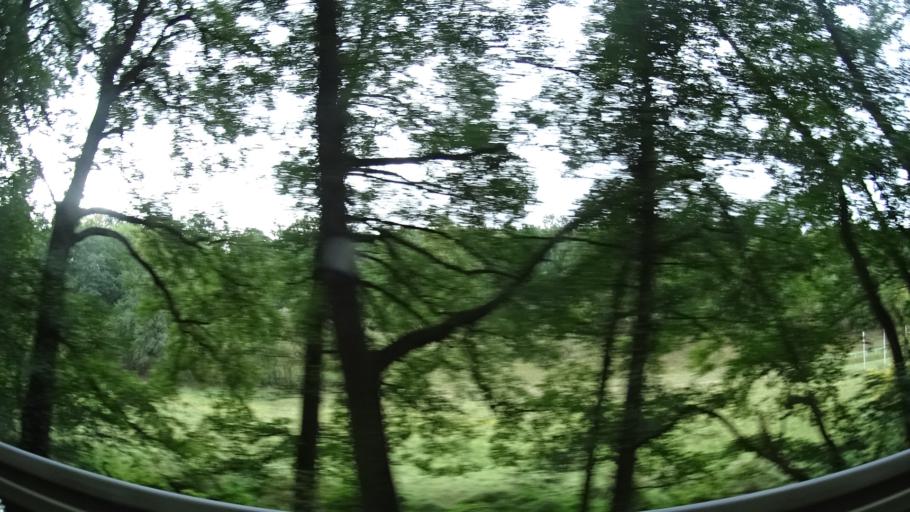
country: DE
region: Thuringia
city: Wahns
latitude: 50.6287
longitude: 10.3121
